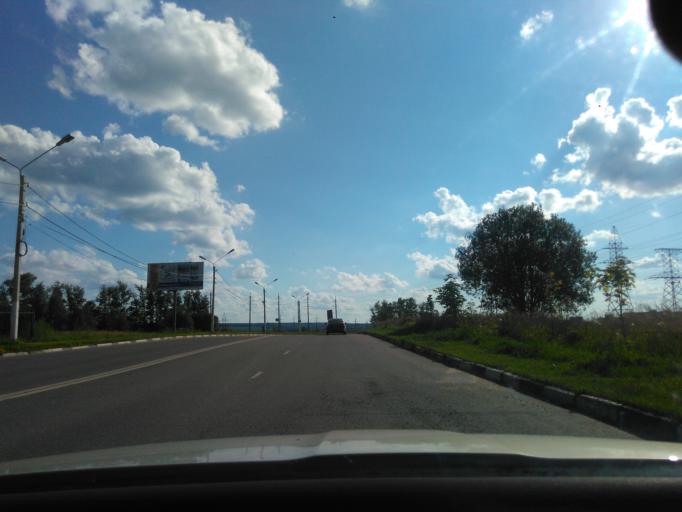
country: RU
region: Moskovskaya
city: Klin
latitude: 56.3174
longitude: 36.7509
